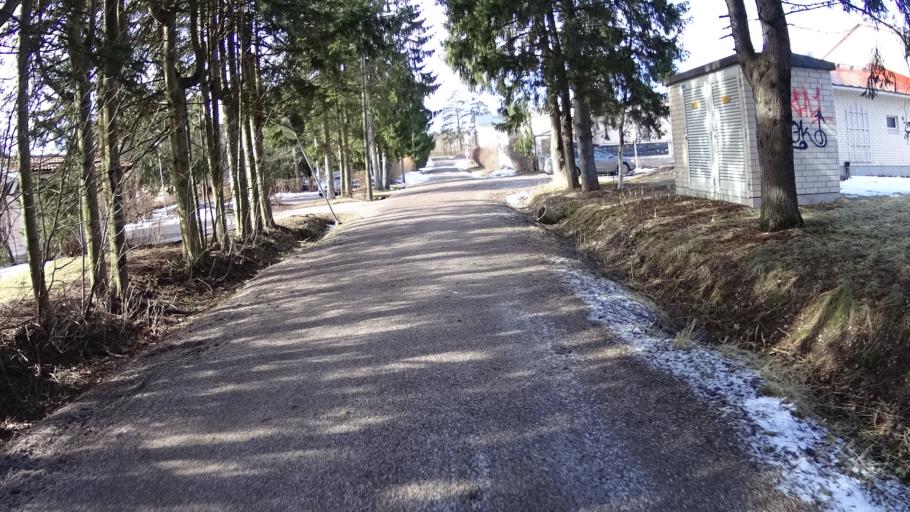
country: FI
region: Uusimaa
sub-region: Helsinki
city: Kilo
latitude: 60.2329
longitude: 24.8166
